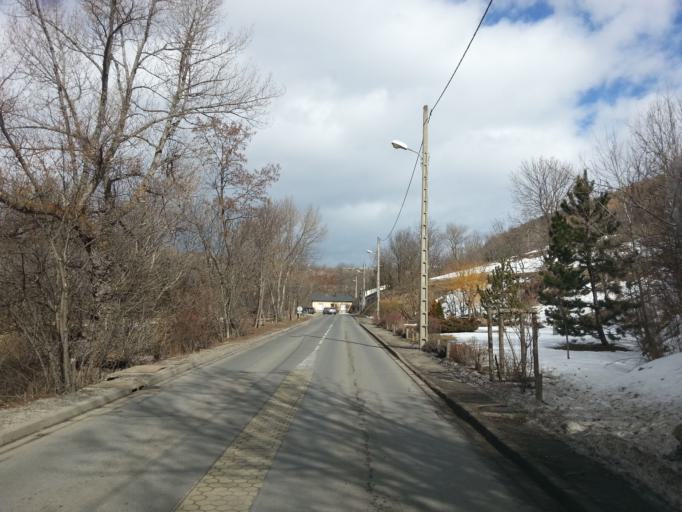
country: ES
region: Catalonia
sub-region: Provincia de Girona
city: Llivia
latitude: 42.4601
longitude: 2.0409
